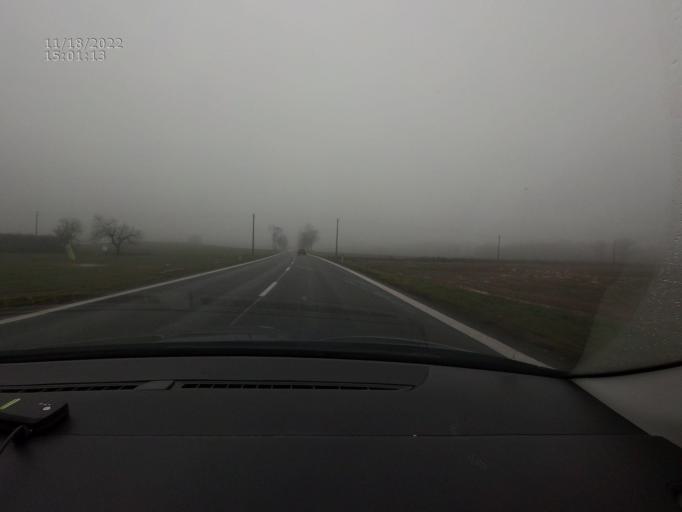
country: CZ
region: Jihocesky
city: Kovarov
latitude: 49.5048
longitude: 14.2096
